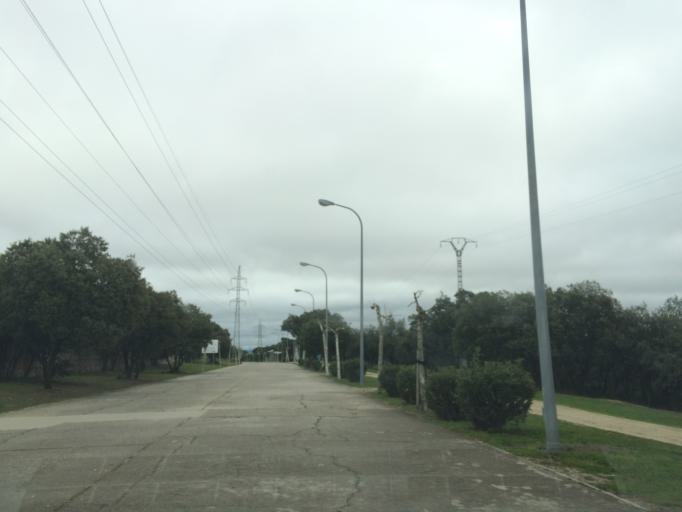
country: ES
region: Madrid
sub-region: Provincia de Madrid
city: Tres Cantos
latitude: 40.5785
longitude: -3.7028
